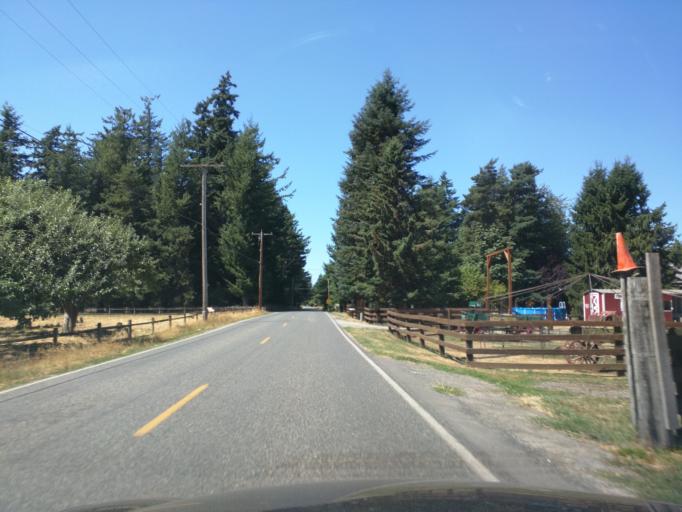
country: US
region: Washington
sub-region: Whatcom County
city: Lynden
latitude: 48.9136
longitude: -122.4381
